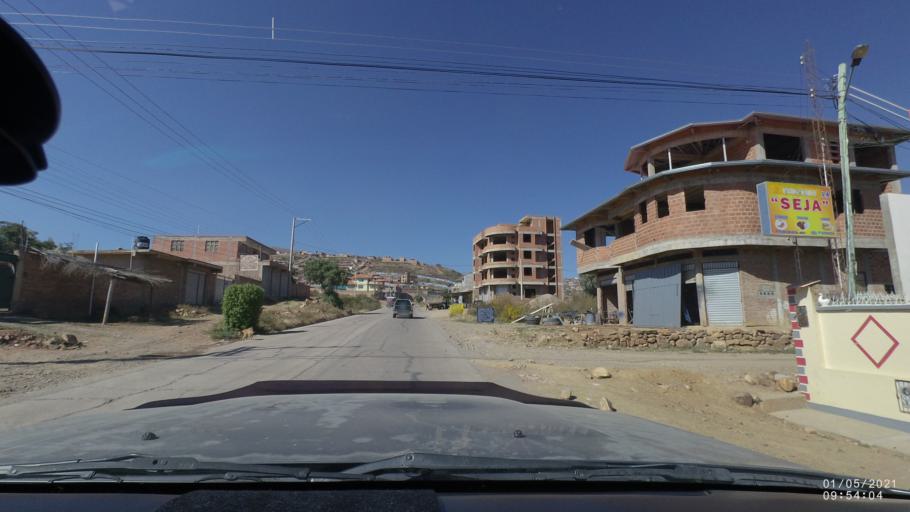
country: BO
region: Cochabamba
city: Cochabamba
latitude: -17.4884
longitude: -66.1726
